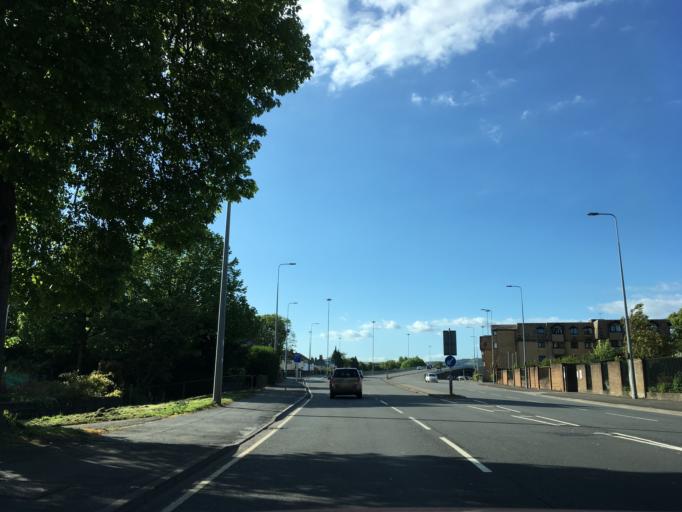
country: GB
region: Wales
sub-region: Cardiff
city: Cardiff
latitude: 51.5016
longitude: -3.1963
